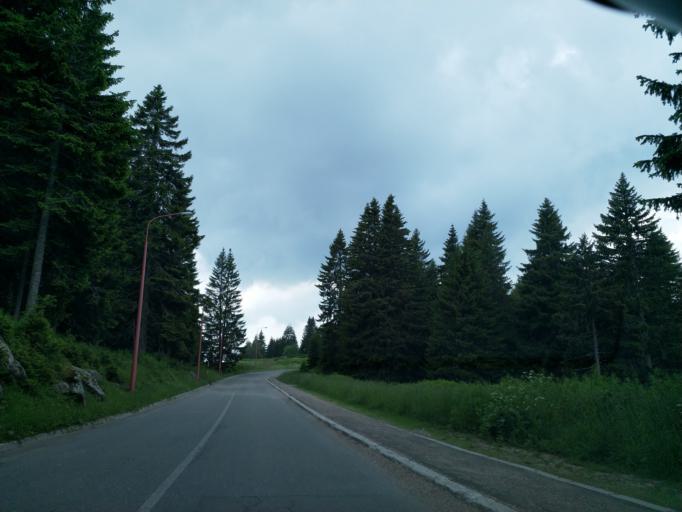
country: XK
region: Mitrovica
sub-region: Komuna e Leposaviqit
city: Leposaviq
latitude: 43.2865
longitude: 20.8007
